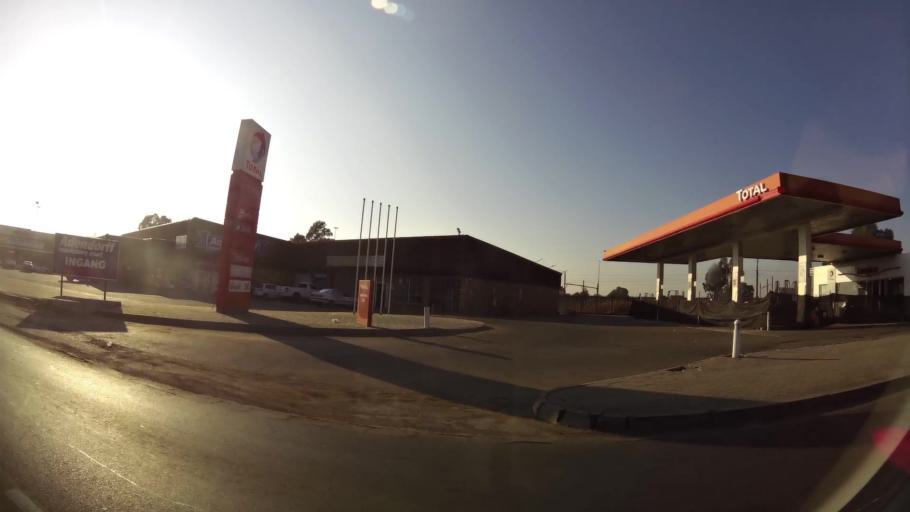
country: ZA
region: Orange Free State
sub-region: Mangaung Metropolitan Municipality
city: Bloemfontein
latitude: -29.1369
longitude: 26.2168
